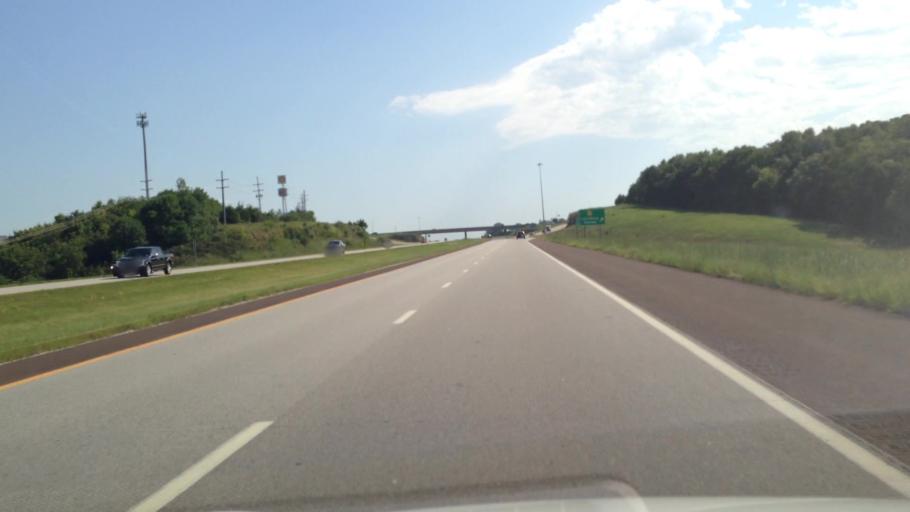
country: US
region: Kansas
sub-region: Miami County
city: Louisburg
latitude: 38.6271
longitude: -94.6949
